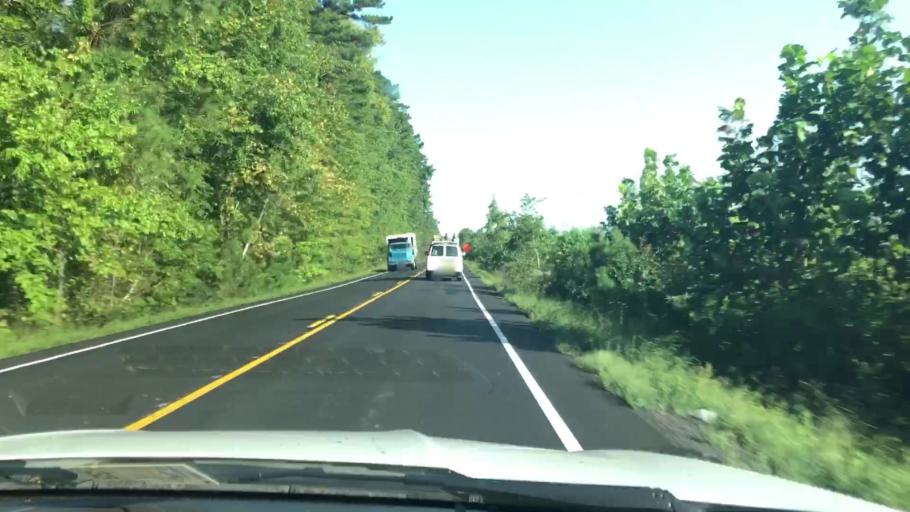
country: US
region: Virginia
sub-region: King William County
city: West Point
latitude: 37.4726
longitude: -76.8453
